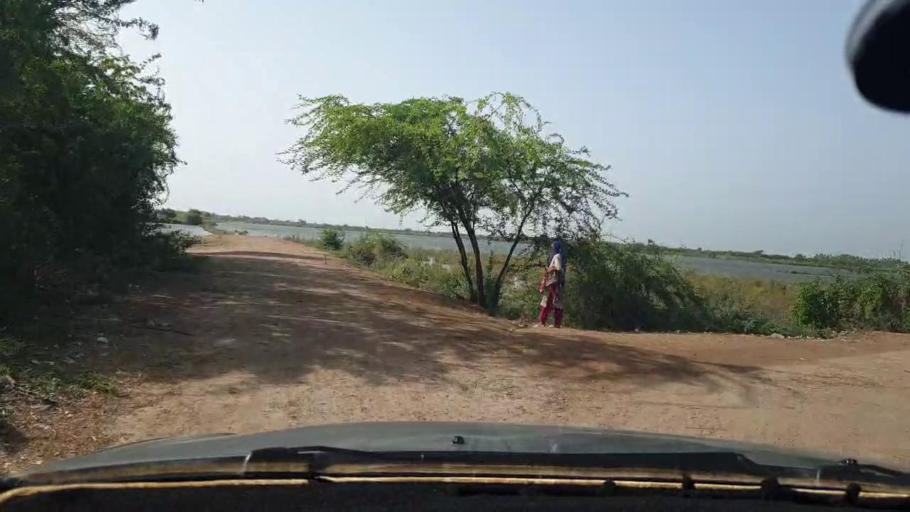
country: PK
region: Sindh
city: Tando Bago
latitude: 24.8055
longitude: 68.9163
